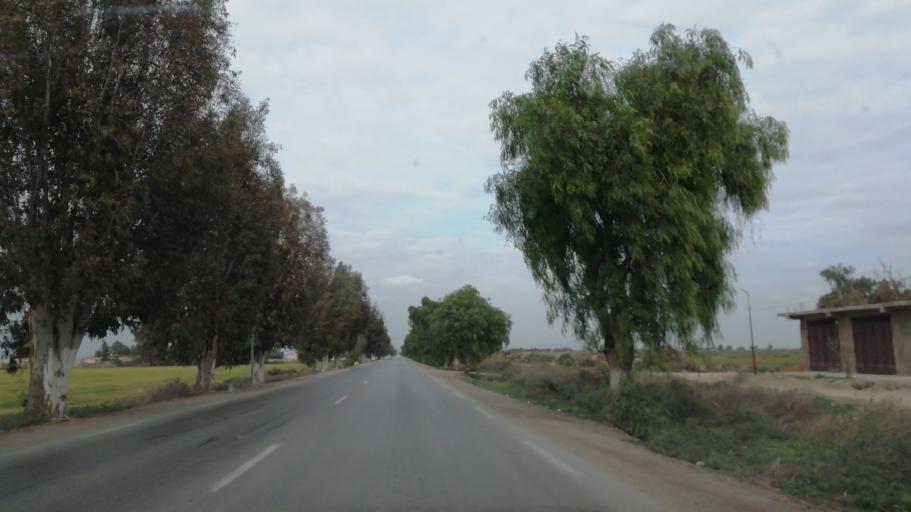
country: DZ
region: Mascara
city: Mascara
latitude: 35.6329
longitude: 0.0611
